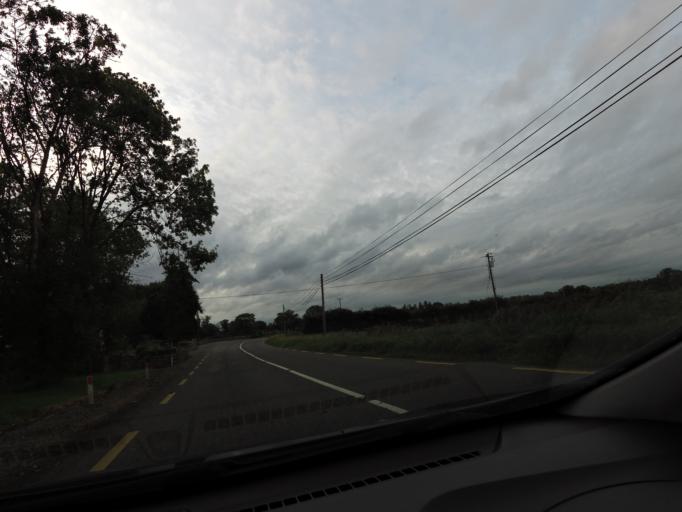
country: IE
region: Leinster
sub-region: Uibh Fhaili
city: Ferbane
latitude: 53.3612
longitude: -7.8510
